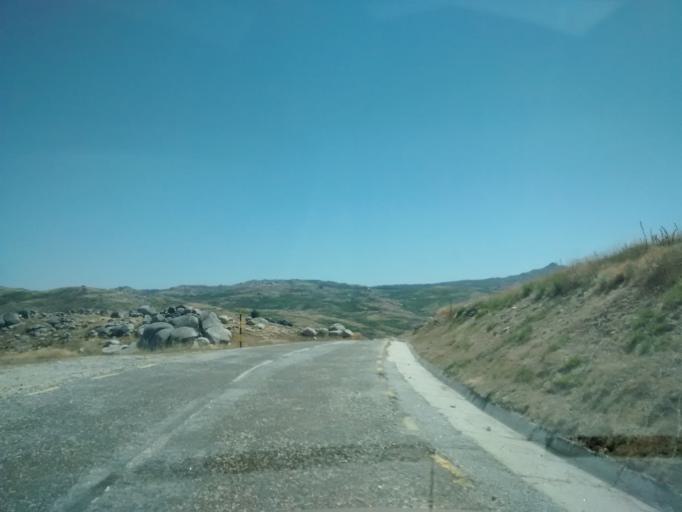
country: PT
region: Guarda
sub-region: Seia
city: Seia
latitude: 40.4207
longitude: -7.6315
